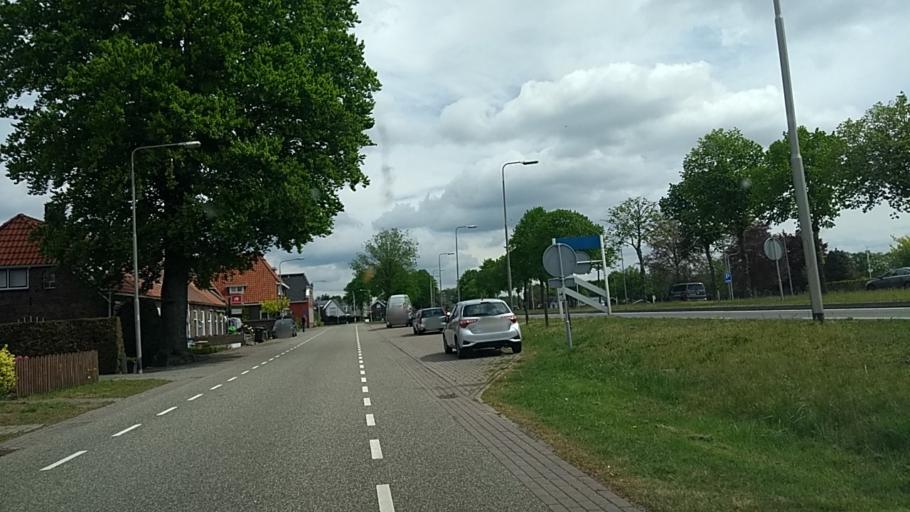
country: NL
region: Overijssel
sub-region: Gemeente Staphorst
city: Staphorst
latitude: 52.5925
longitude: 6.2636
